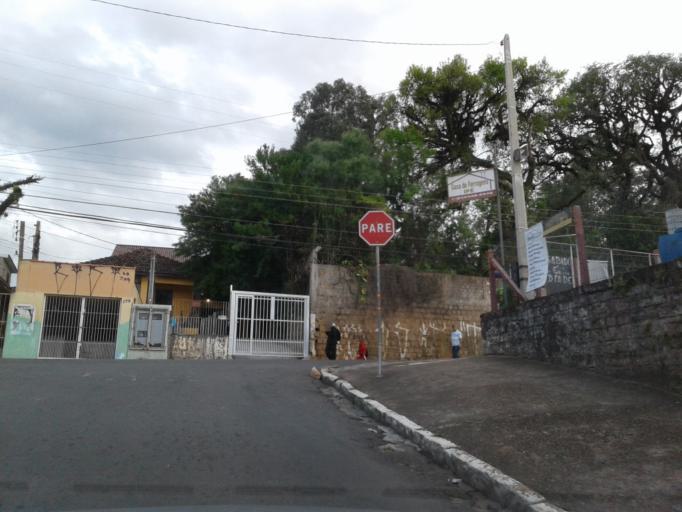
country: BR
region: Rio Grande do Sul
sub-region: Porto Alegre
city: Porto Alegre
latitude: -30.0591
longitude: -51.1464
